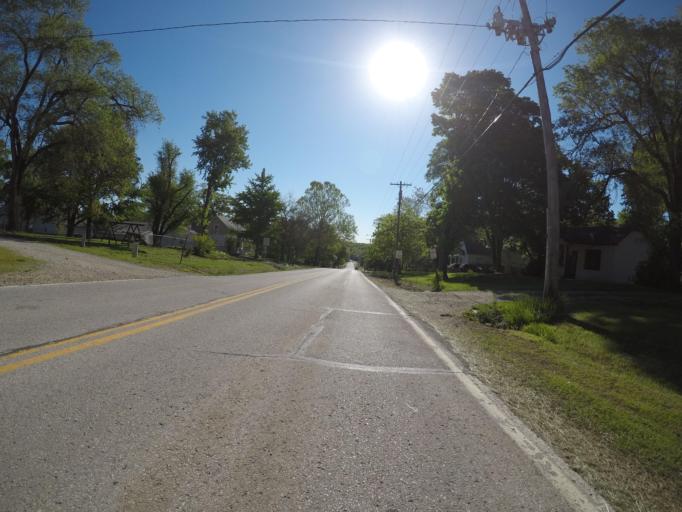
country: US
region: Kansas
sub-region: Douglas County
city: Lawrence
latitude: 39.0440
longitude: -95.3965
